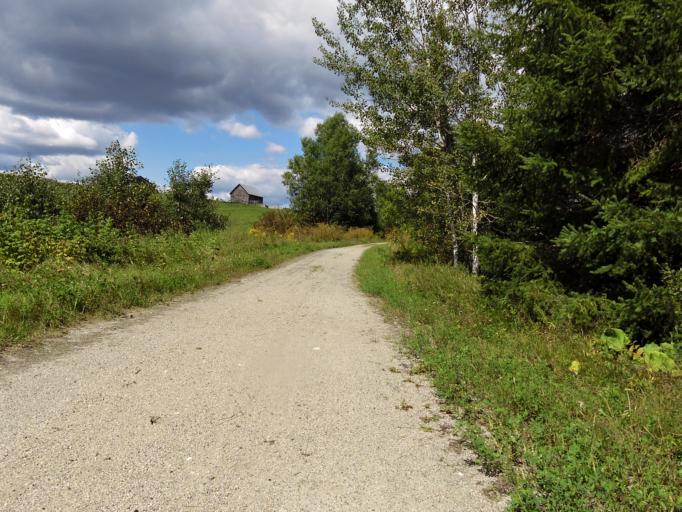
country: CA
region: Quebec
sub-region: Outaouais
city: Wakefield
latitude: 45.8242
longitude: -75.9785
